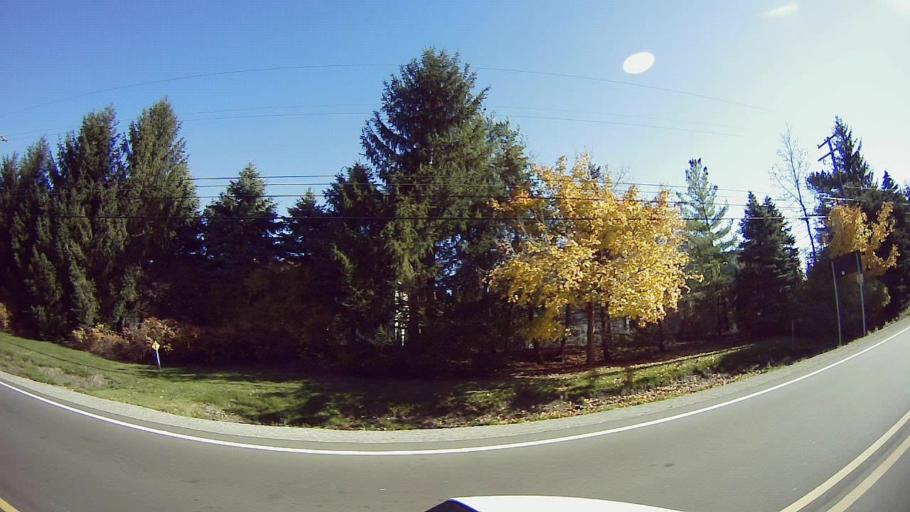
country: US
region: Michigan
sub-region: Oakland County
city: Bingham Farms
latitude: 42.5149
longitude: -83.2621
